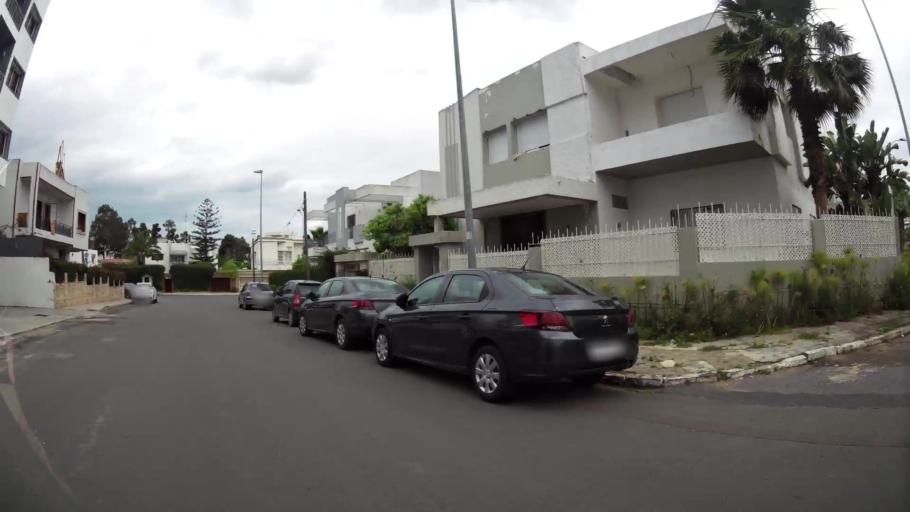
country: MA
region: Grand Casablanca
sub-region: Casablanca
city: Casablanca
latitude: 33.5637
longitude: -7.6419
